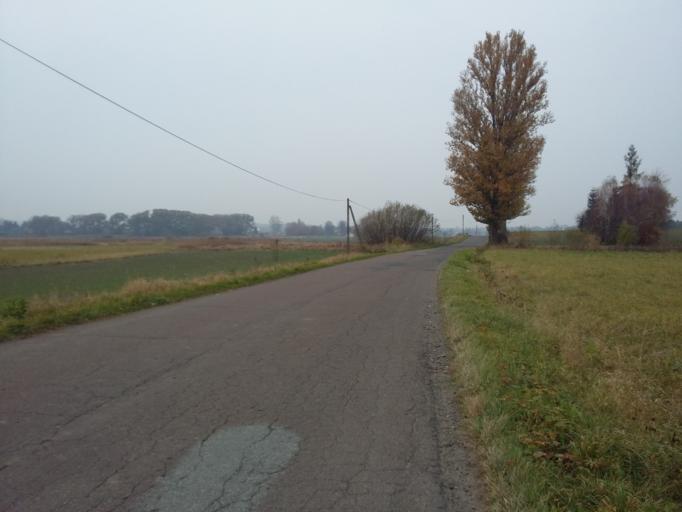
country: PL
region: Subcarpathian Voivodeship
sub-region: Powiat jasielski
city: Tarnowiec
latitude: 49.7299
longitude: 21.5685
